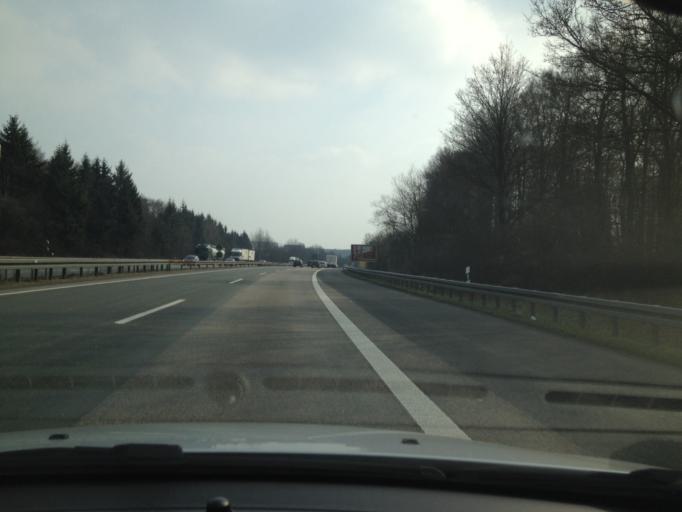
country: DE
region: North Rhine-Westphalia
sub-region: Regierungsbezirk Arnsberg
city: Wilnsdorf
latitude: 50.7798
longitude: 8.1483
